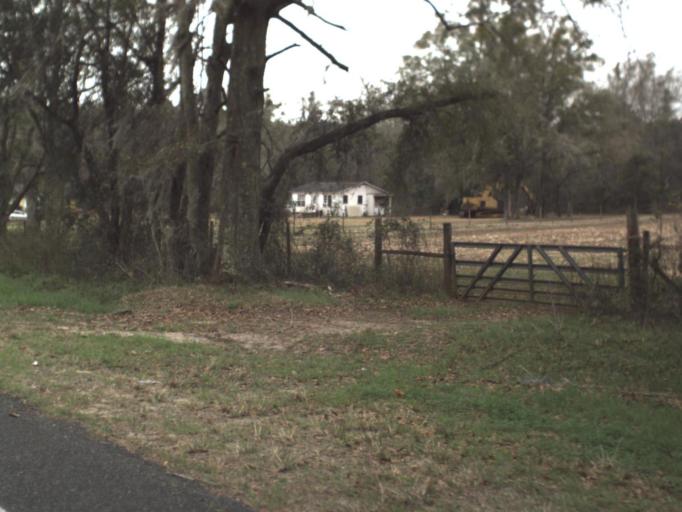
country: US
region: Florida
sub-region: Leon County
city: Tallahassee
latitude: 30.4235
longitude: -84.1732
